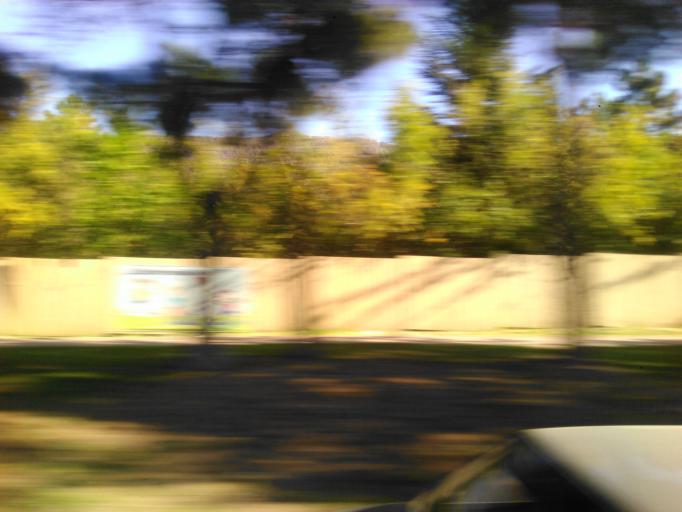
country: RU
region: Krasnodarskiy
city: Gelendzhik
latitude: 44.5814
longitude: 38.0645
